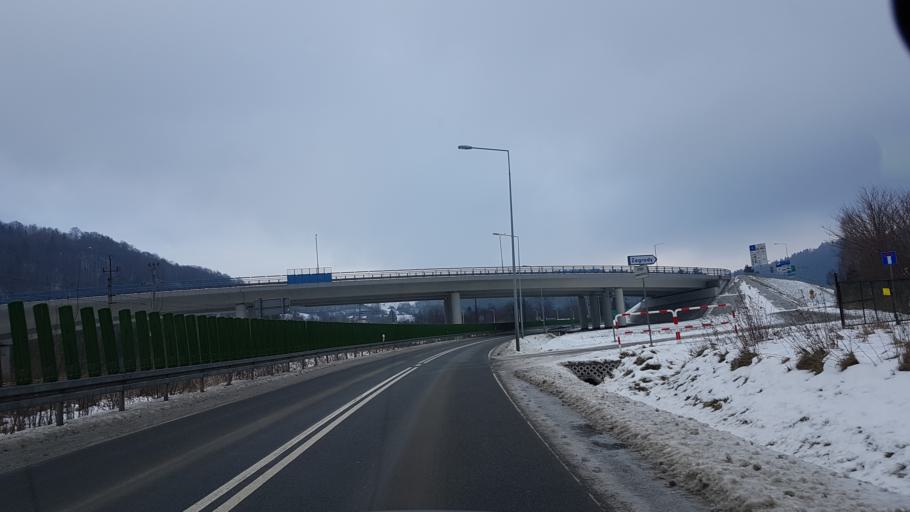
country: PL
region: Lesser Poland Voivodeship
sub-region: Powiat nowosadecki
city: Piwniczna-Zdroj
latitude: 49.4172
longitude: 20.7266
